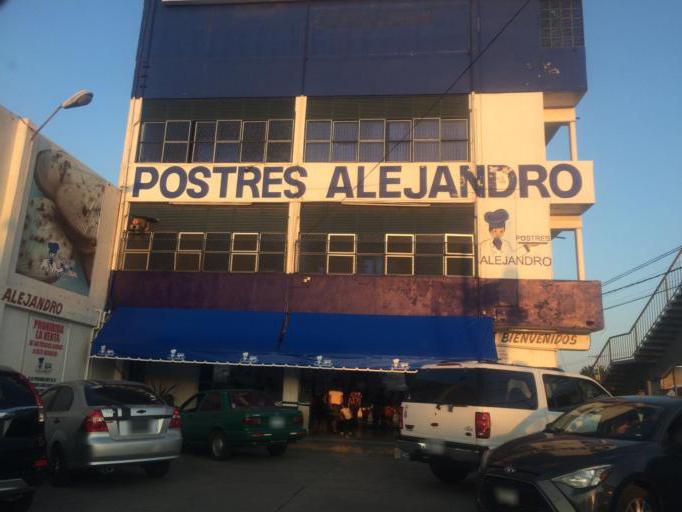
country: MX
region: Guanajuato
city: Leon
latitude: 21.0970
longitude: -101.6503
